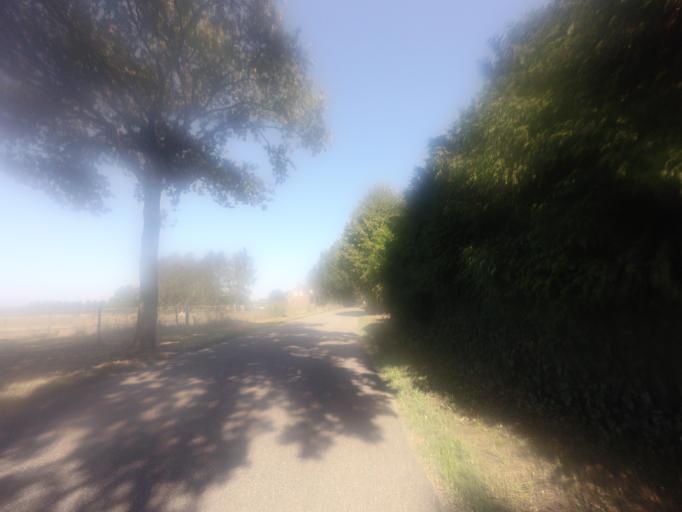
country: NL
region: North Brabant
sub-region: Gemeente Veldhoven
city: Oerle
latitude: 51.4473
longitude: 5.3400
